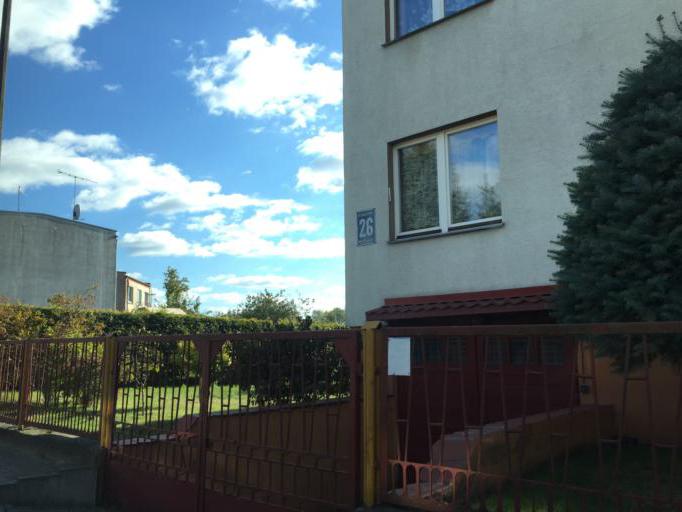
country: PL
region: Warmian-Masurian Voivodeship
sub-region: Powiat bartoszycki
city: Bartoszyce
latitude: 54.2431
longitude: 20.8162
